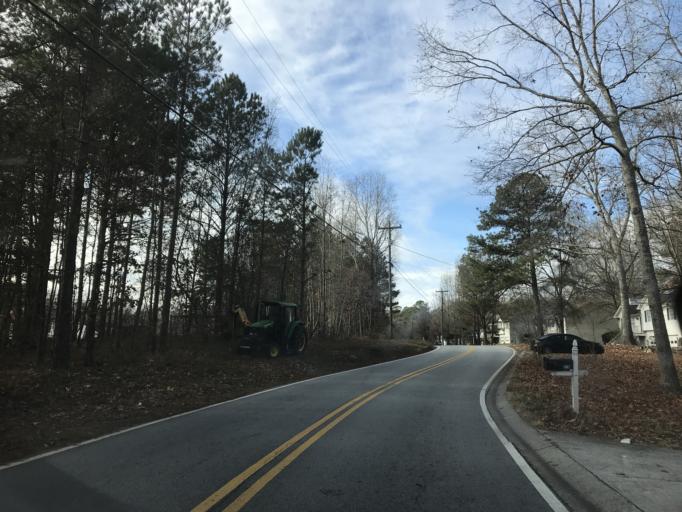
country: US
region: Georgia
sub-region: Douglas County
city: Douglasville
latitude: 33.7960
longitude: -84.8229
